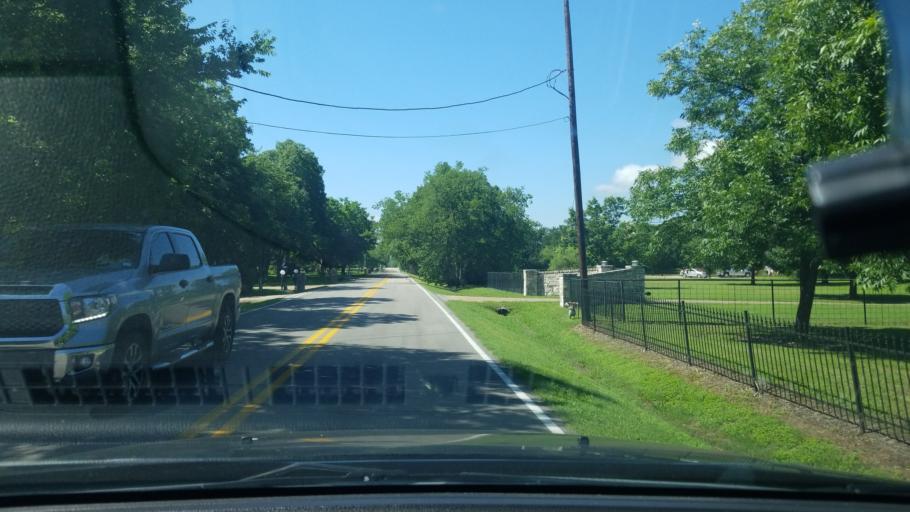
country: US
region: Texas
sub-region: Dallas County
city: Sunnyvale
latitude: 32.7890
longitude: -96.5550
